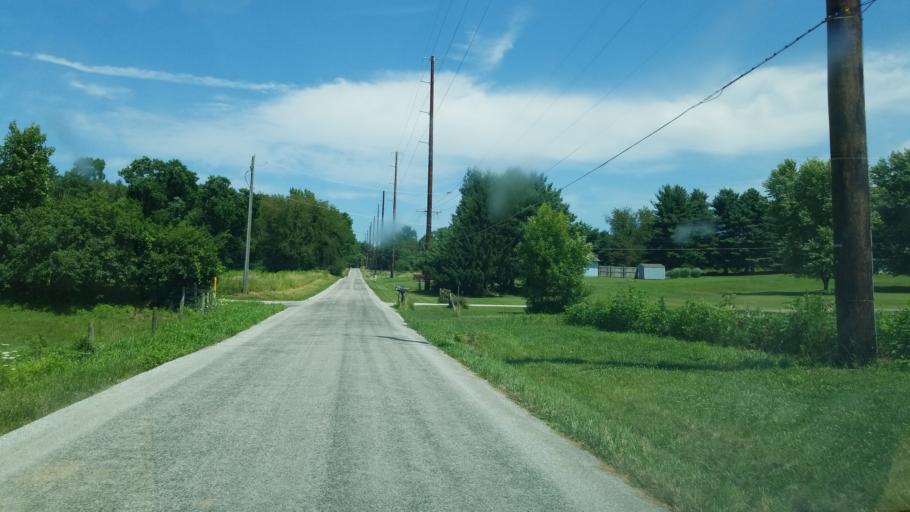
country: US
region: Ohio
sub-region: Ashland County
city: Ashland
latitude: 40.8863
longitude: -82.2689
